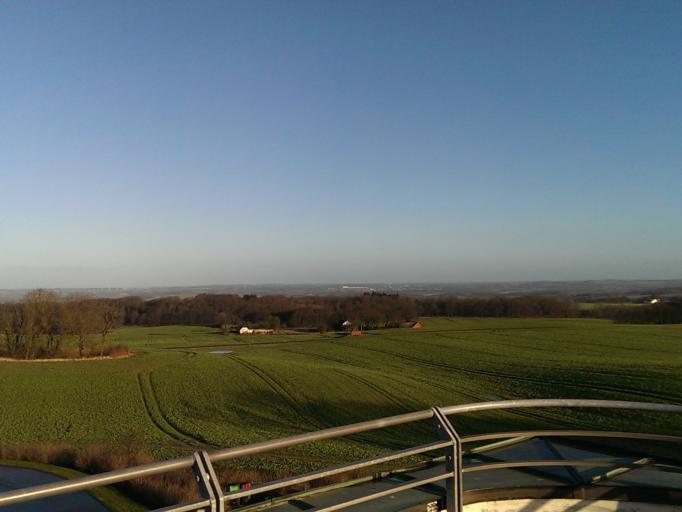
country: DK
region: Central Jutland
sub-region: Skanderborg Kommune
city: Skanderborg
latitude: 55.9771
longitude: 9.8308
